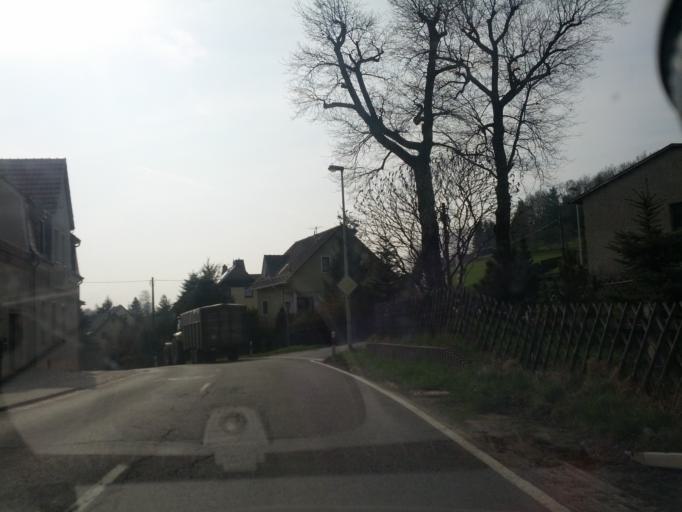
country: DE
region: Saxony
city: Kirchberg
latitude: 50.6247
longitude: 12.5386
